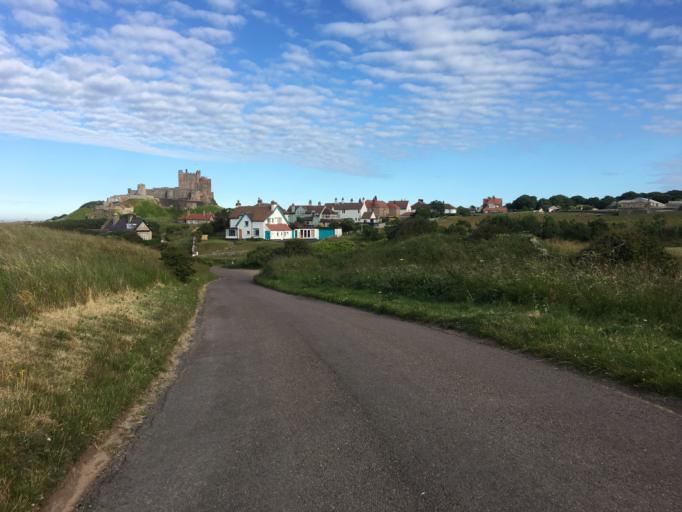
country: GB
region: England
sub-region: Northumberland
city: Bamburgh
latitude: 55.6118
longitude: -1.7193
